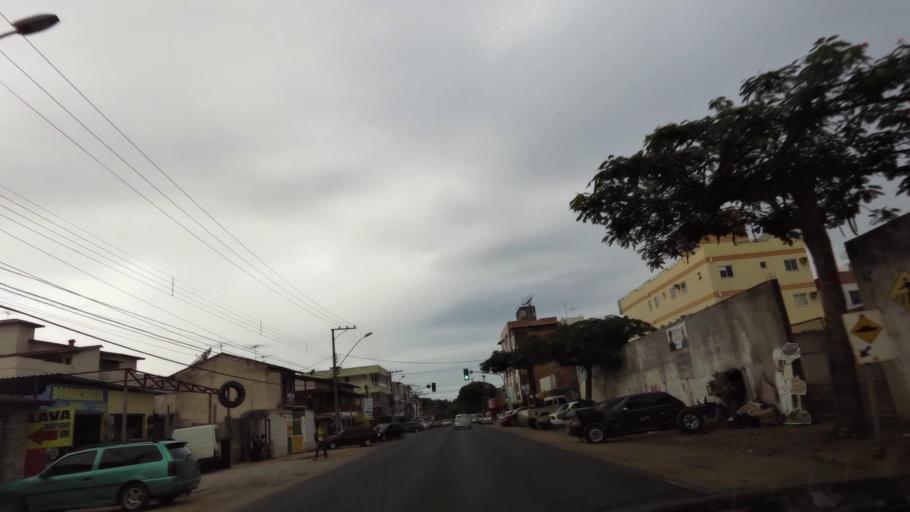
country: BR
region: Espirito Santo
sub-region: Guarapari
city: Guarapari
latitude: -20.7371
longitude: -40.5422
